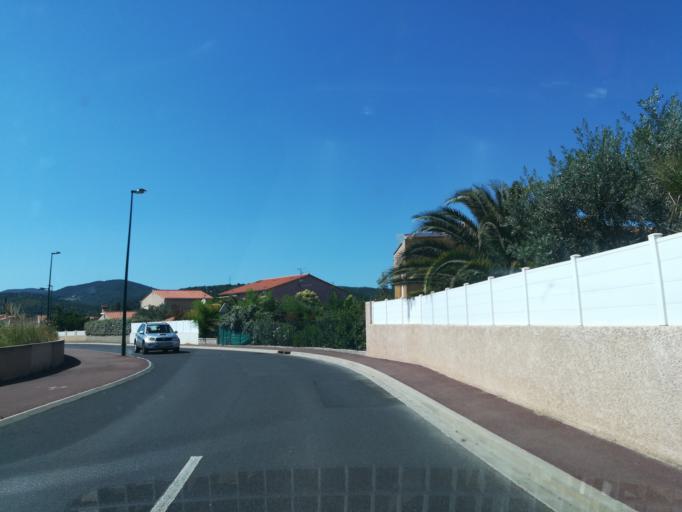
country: FR
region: Languedoc-Roussillon
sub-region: Departement des Pyrenees-Orientales
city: Ceret
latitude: 42.4906
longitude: 2.7415
